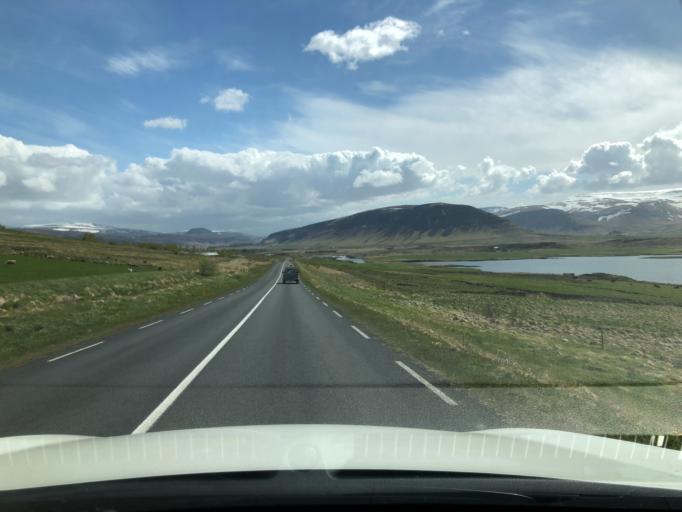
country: IS
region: Capital Region
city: Mosfellsbaer
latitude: 64.3518
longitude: -21.6358
